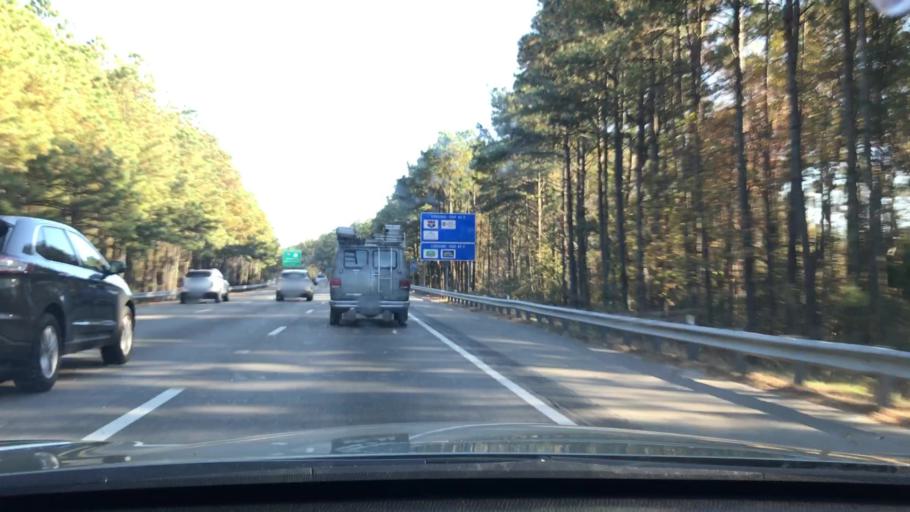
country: US
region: Virginia
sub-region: Henrico County
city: Glen Allen
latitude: 37.6623
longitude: -77.4769
